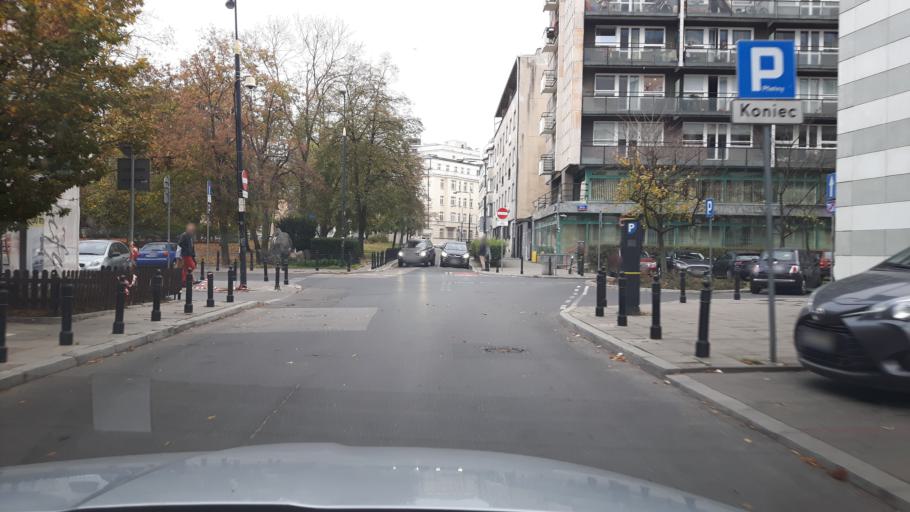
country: PL
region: Masovian Voivodeship
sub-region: Warszawa
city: Srodmiescie
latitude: 52.2282
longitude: 21.0259
